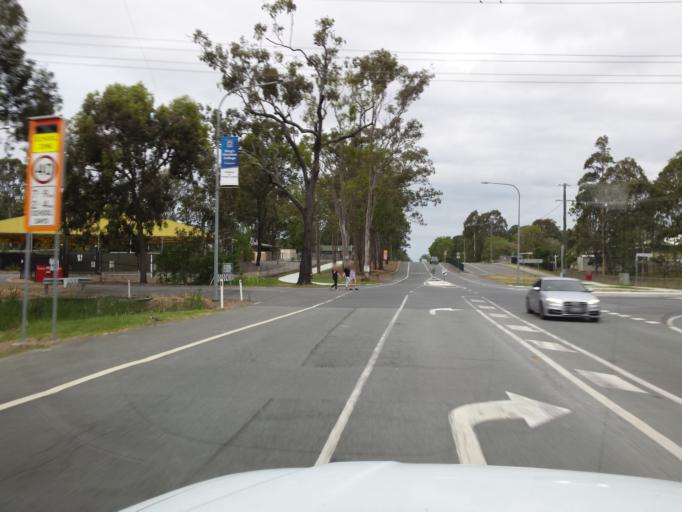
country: AU
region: Queensland
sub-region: Gold Coast
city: Oxenford
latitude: -27.8665
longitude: 153.3149
